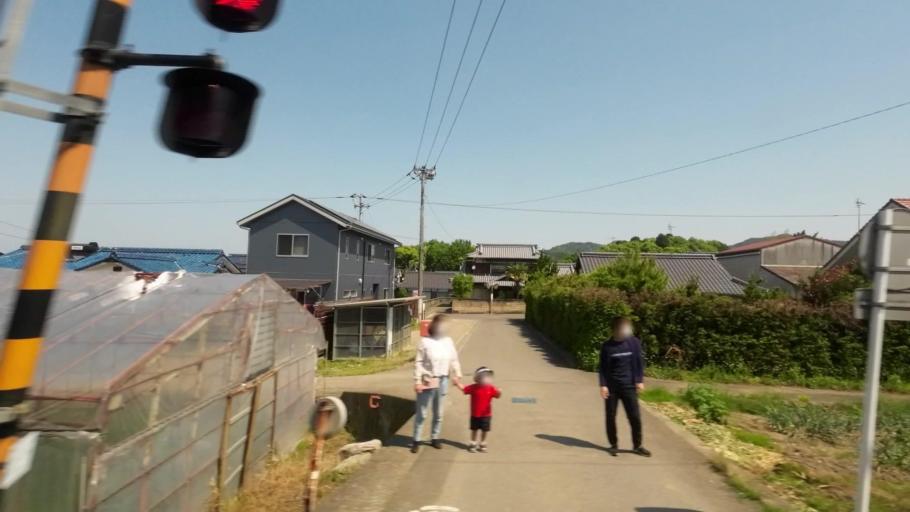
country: JP
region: Ehime
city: Saijo
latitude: 33.9218
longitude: 133.2238
